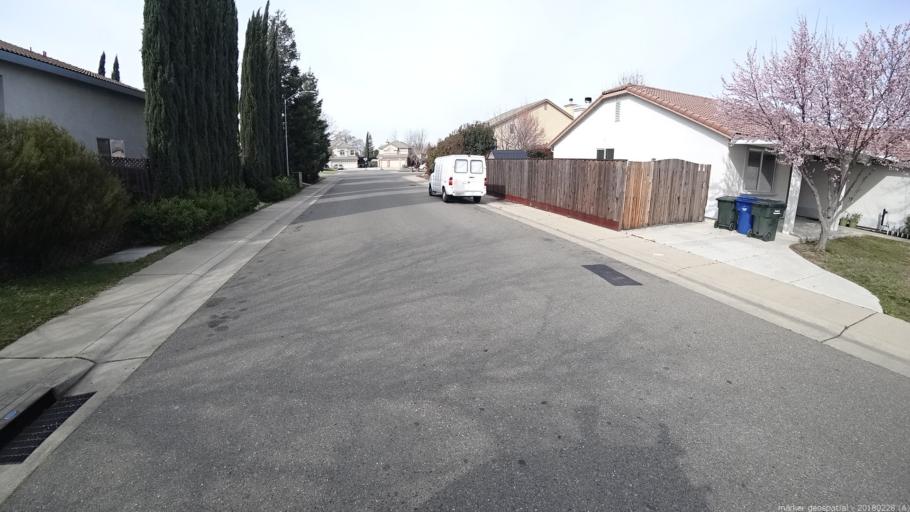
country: US
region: California
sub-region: Sacramento County
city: Antelope
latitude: 38.7187
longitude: -121.3361
